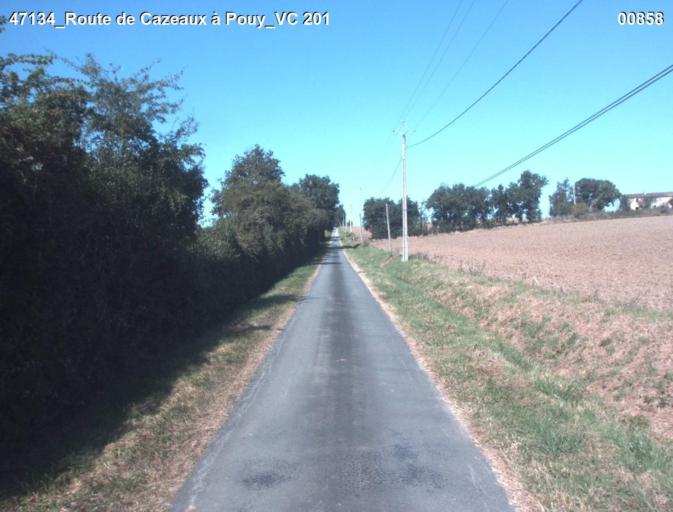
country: FR
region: Aquitaine
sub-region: Departement du Lot-et-Garonne
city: Mezin
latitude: 44.0150
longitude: 0.3011
